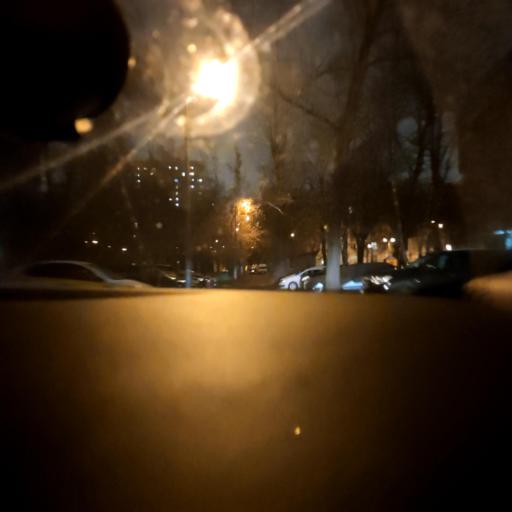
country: RU
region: Moscow
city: Kuz'minki
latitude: 55.6984
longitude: 37.7824
